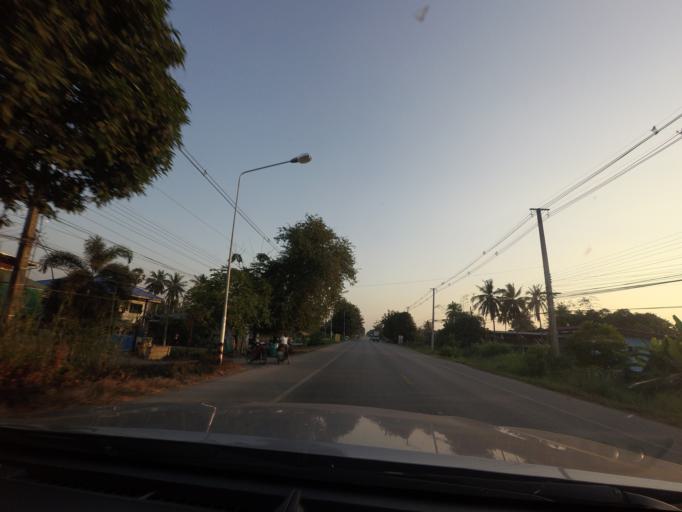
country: TH
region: Sukhothai
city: Si Samrong
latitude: 17.1341
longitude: 99.8501
